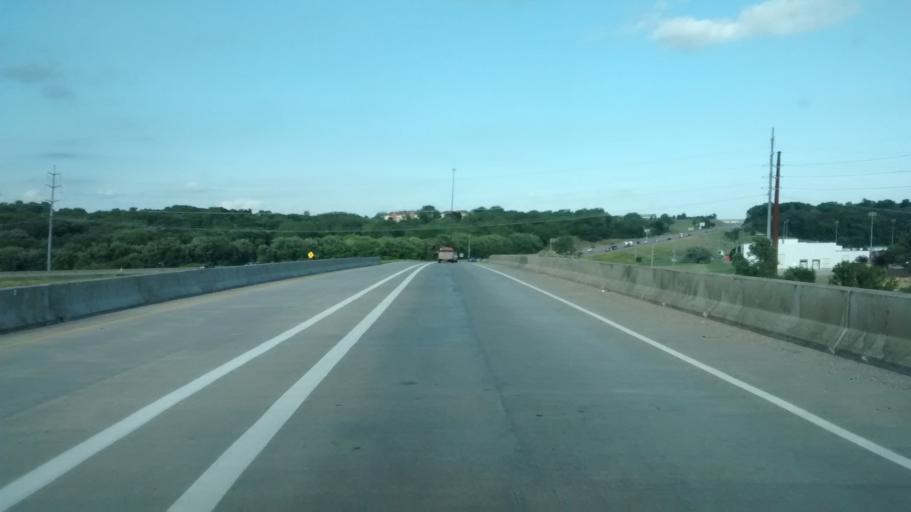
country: US
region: Iowa
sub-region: Woodbury County
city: Sergeant Bluff
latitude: 42.4446
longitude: -96.3719
